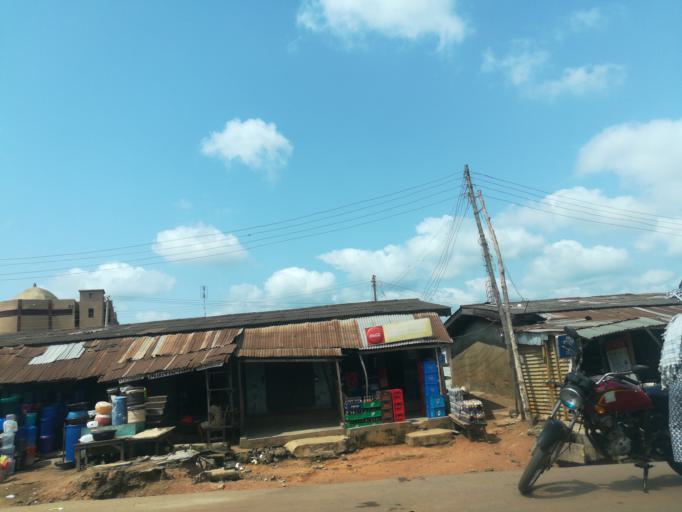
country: NG
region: Oyo
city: Moniya
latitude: 7.5296
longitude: 3.9115
